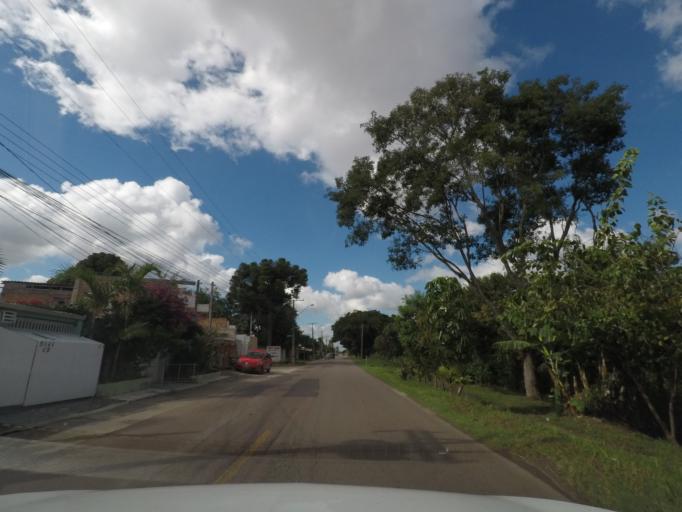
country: BR
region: Parana
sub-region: Curitiba
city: Curitiba
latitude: -25.4745
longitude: -49.2434
